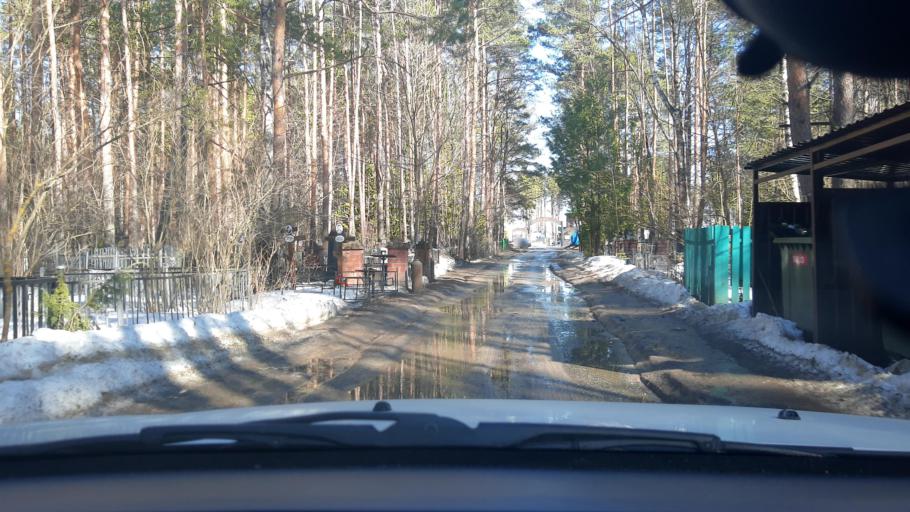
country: RU
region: Nizjnij Novgorod
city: Pyra
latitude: 56.2406
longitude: 43.3688
